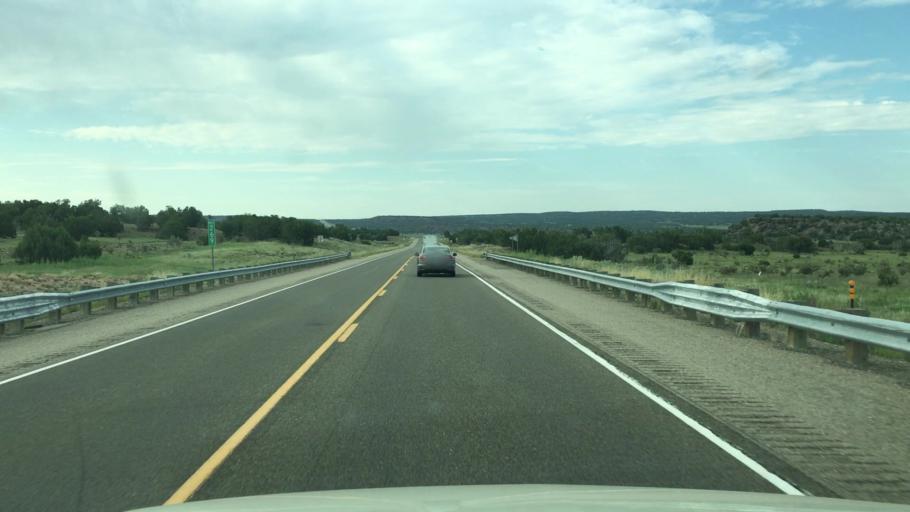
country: US
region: New Mexico
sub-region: Santa Fe County
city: Eldorado at Santa Fe
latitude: 35.2649
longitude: -105.8090
